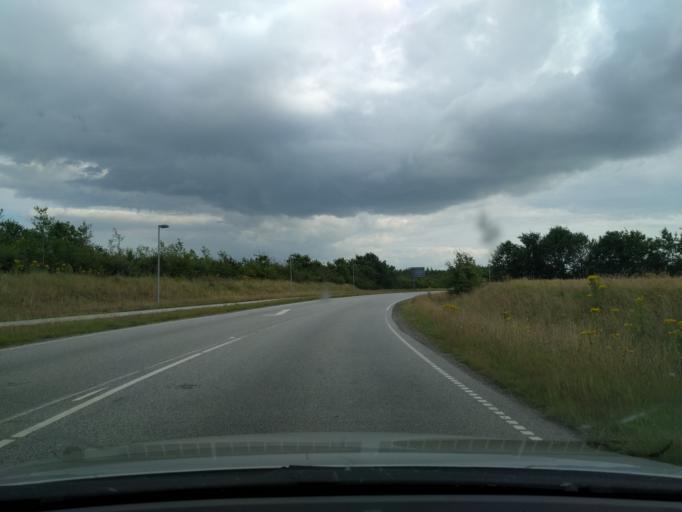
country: DK
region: Central Jutland
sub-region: Herning Kommune
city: Snejbjerg
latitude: 56.1172
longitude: 8.9068
